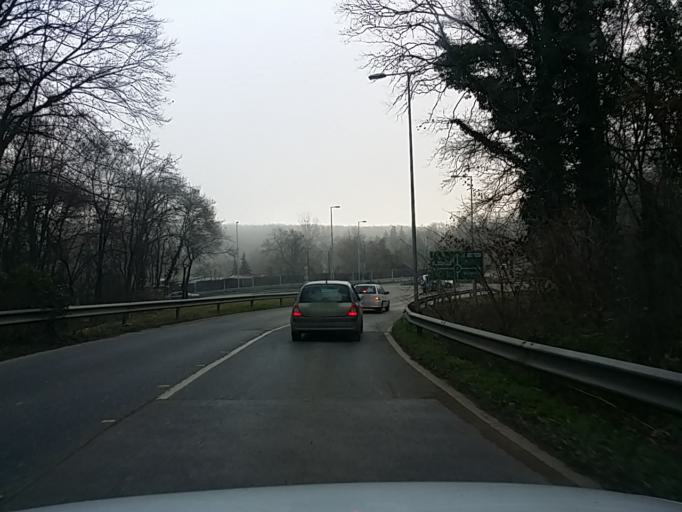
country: HU
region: Pest
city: Budakeszi
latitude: 47.5424
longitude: 18.9499
